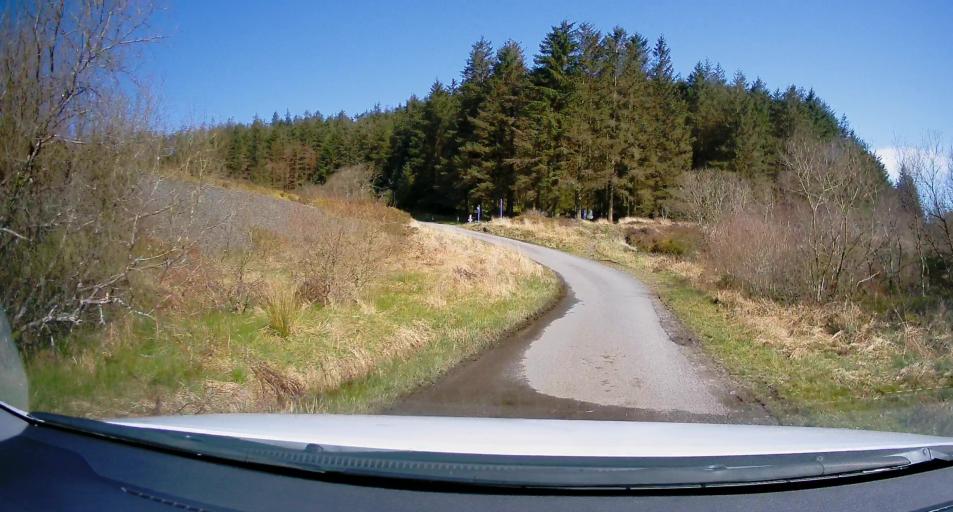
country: GB
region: Wales
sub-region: County of Ceredigion
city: Bow Street
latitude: 52.4372
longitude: -3.8996
